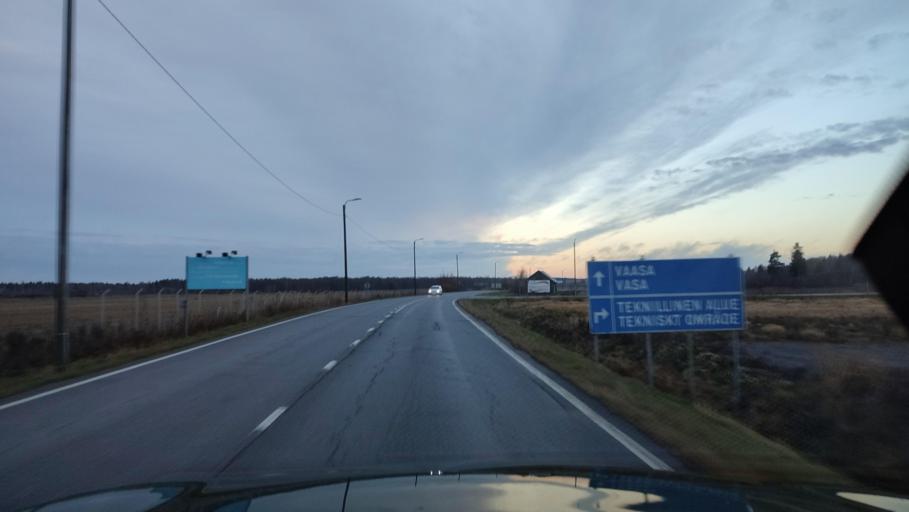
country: FI
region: Ostrobothnia
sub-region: Vaasa
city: Ristinummi
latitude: 63.0436
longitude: 21.7551
